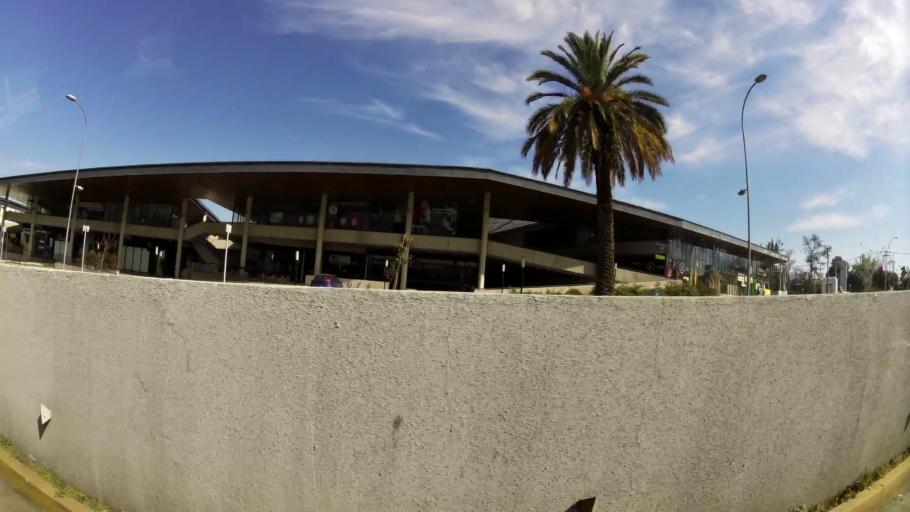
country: CL
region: Santiago Metropolitan
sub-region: Provincia de Santiago
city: Villa Presidente Frei, Nunoa, Santiago, Chile
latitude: -33.4404
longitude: -70.5357
